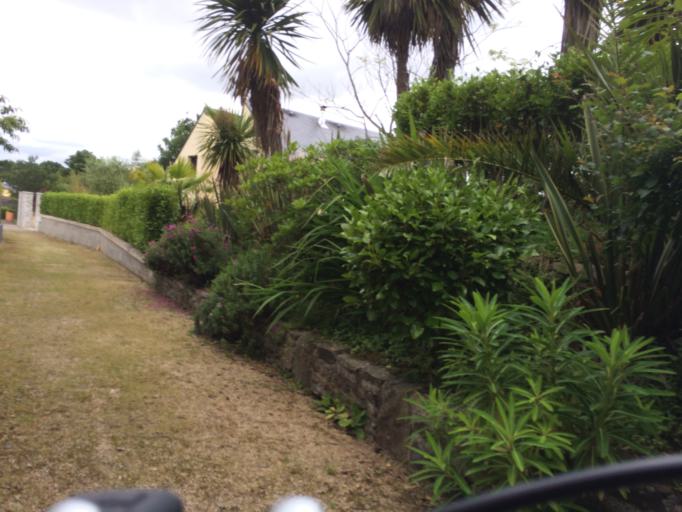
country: FR
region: Brittany
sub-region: Departement du Finistere
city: Hopital-Camfrout
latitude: 48.3290
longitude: -4.2496
